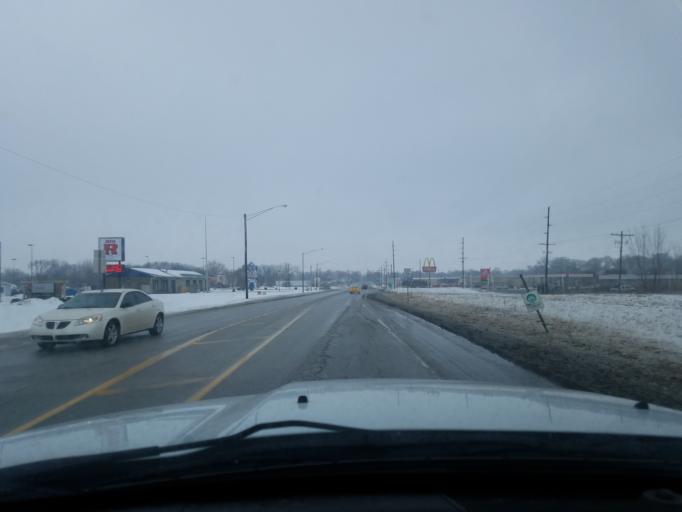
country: US
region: Indiana
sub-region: Fulton County
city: Rochester
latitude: 41.0497
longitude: -86.2186
